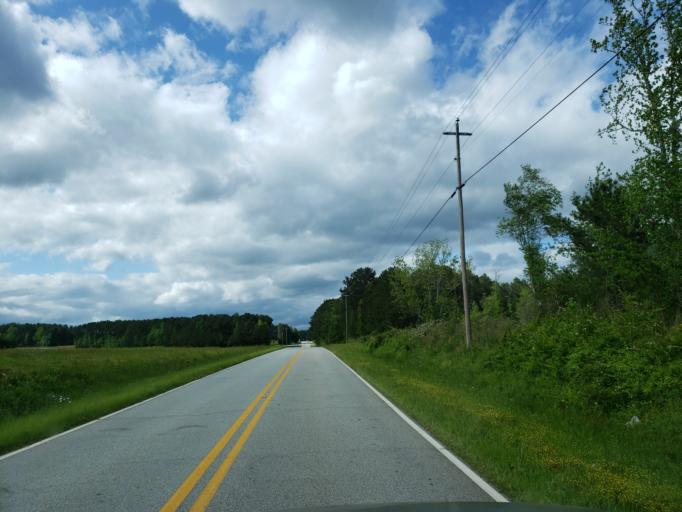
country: US
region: Georgia
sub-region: Carroll County
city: Mount Zion
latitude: 33.6832
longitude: -85.1873
